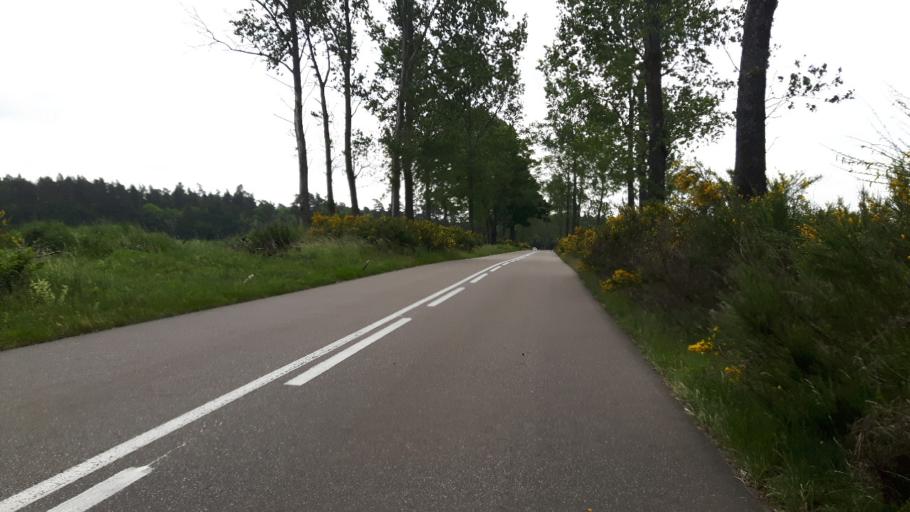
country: PL
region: Pomeranian Voivodeship
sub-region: Powiat leborski
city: Leba
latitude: 54.7473
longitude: 17.7118
